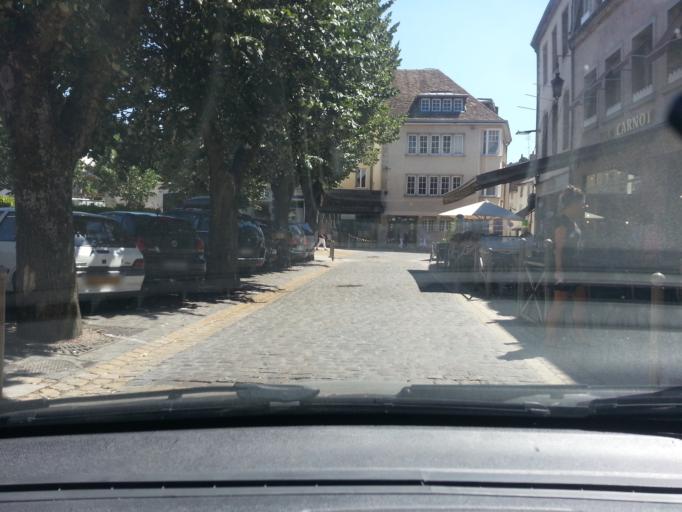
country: FR
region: Bourgogne
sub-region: Departement de la Cote-d'Or
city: Beaune
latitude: 47.0226
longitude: 4.8378
